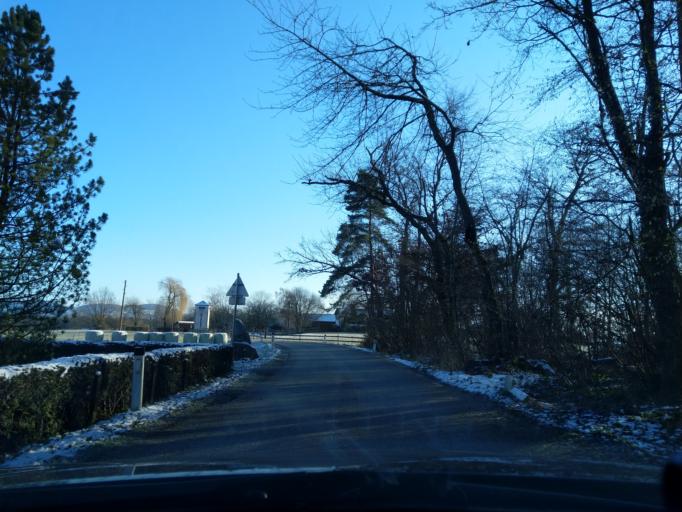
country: AT
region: Upper Austria
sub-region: Politischer Bezirk Urfahr-Umgebung
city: Engerwitzdorf
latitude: 48.3753
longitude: 14.4964
